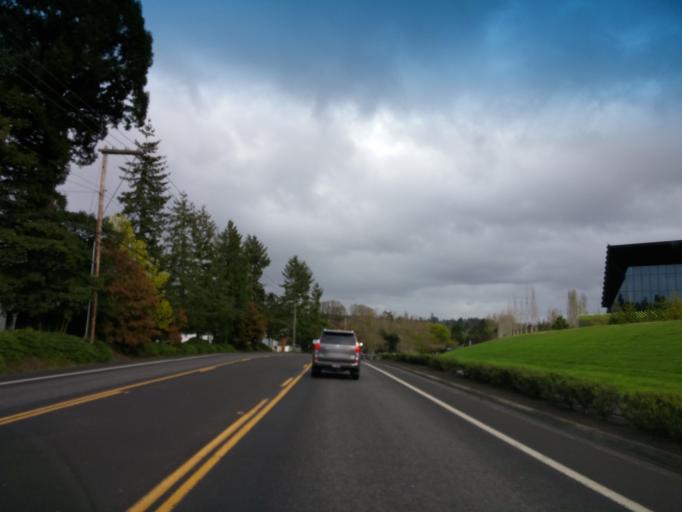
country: US
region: Oregon
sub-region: Washington County
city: Cedar Mill
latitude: 45.5130
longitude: -122.8260
